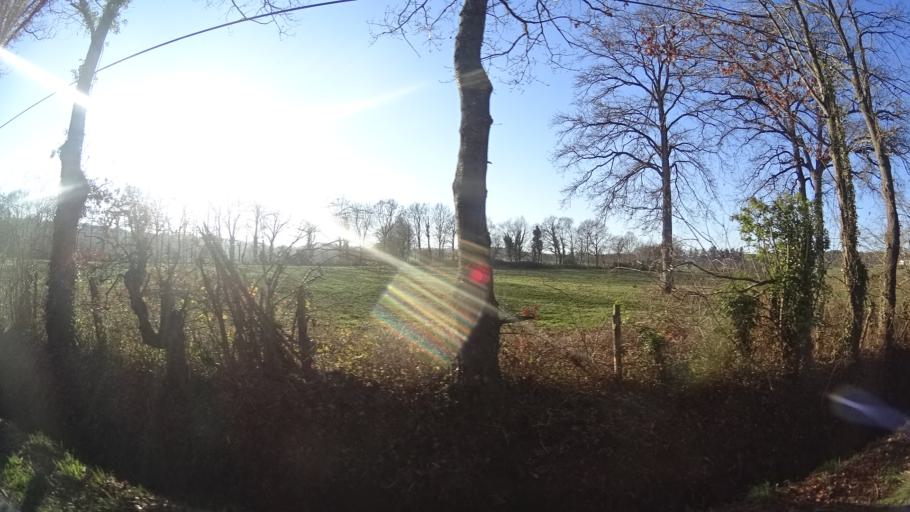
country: FR
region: Brittany
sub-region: Departement du Morbihan
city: Allaire
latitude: 47.6731
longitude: -2.1741
